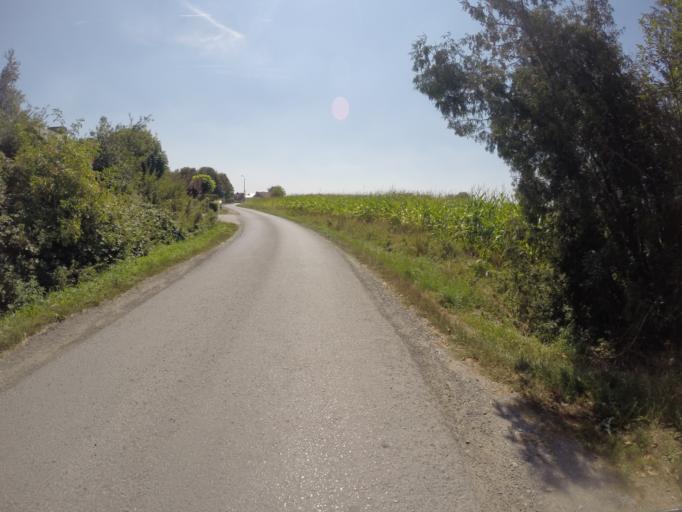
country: BE
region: Flanders
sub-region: Provincie Oost-Vlaanderen
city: Knesselare
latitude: 51.1414
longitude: 3.4409
